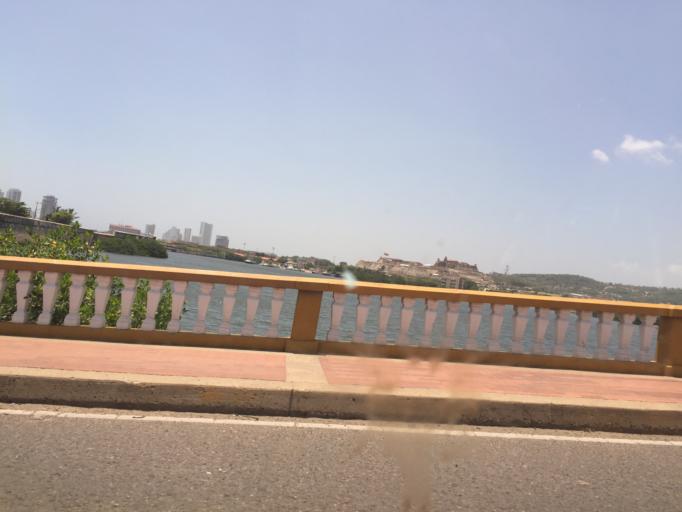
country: CO
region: Bolivar
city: Cartagena
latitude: 10.4175
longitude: -75.5447
